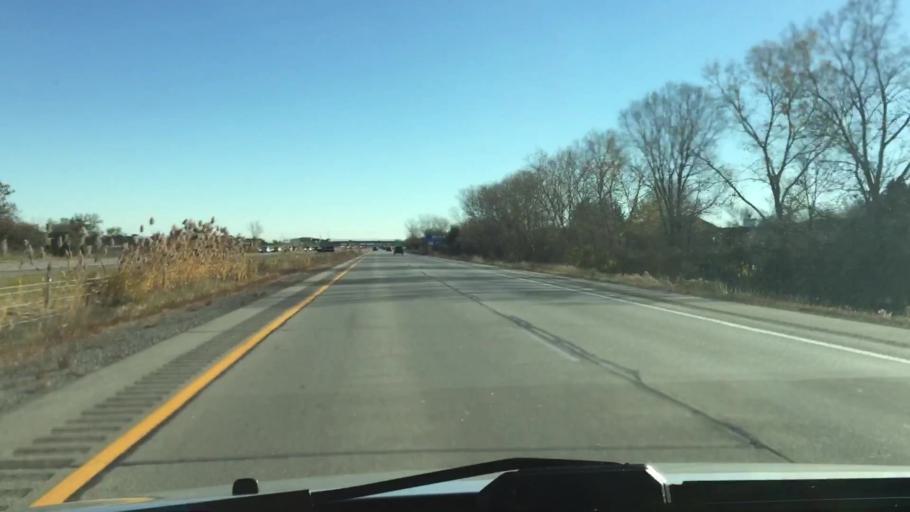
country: US
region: Wisconsin
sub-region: Outagamie County
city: Appleton
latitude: 44.2982
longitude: -88.3879
